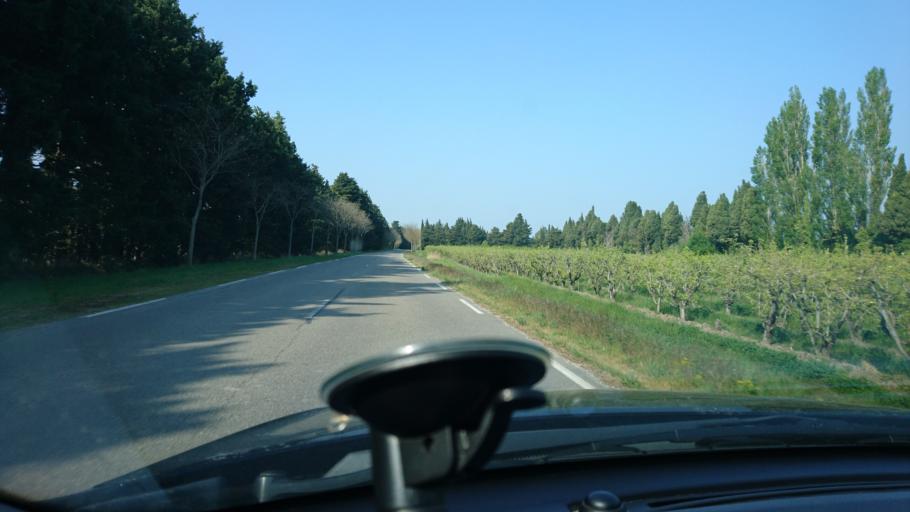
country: FR
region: Provence-Alpes-Cote d'Azur
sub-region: Departement des Bouches-du-Rhone
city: Saint-Andiol
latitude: 43.8381
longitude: 4.9113
